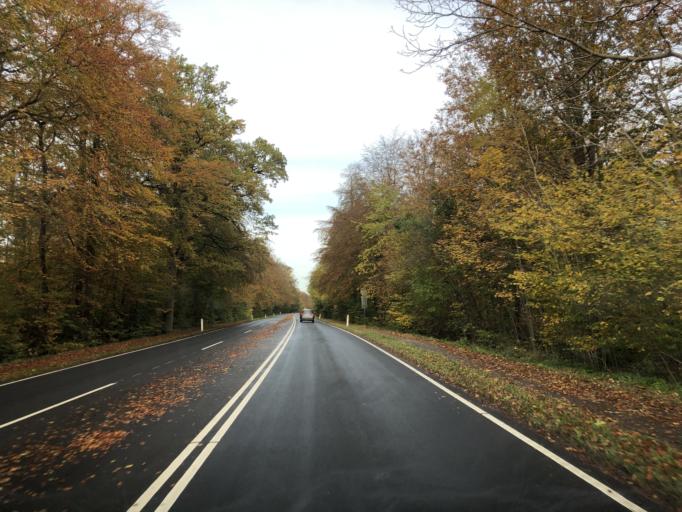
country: DK
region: Capital Region
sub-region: Hillerod Kommune
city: Hillerod
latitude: 55.9252
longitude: 12.3263
